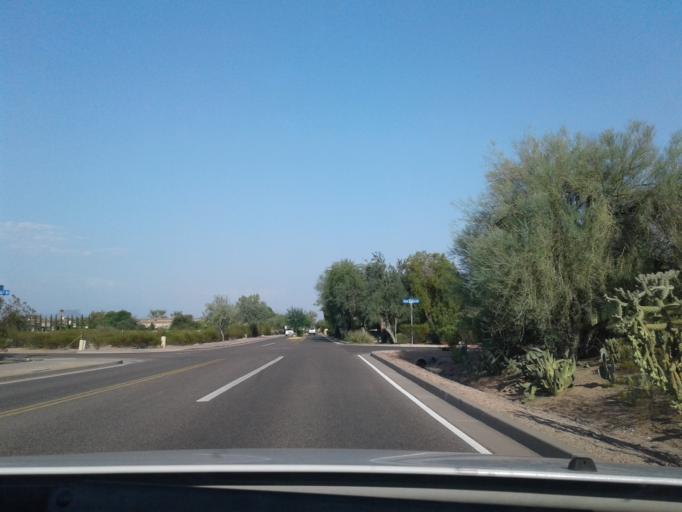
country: US
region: Arizona
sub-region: Maricopa County
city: Paradise Valley
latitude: 33.5238
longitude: -111.9394
